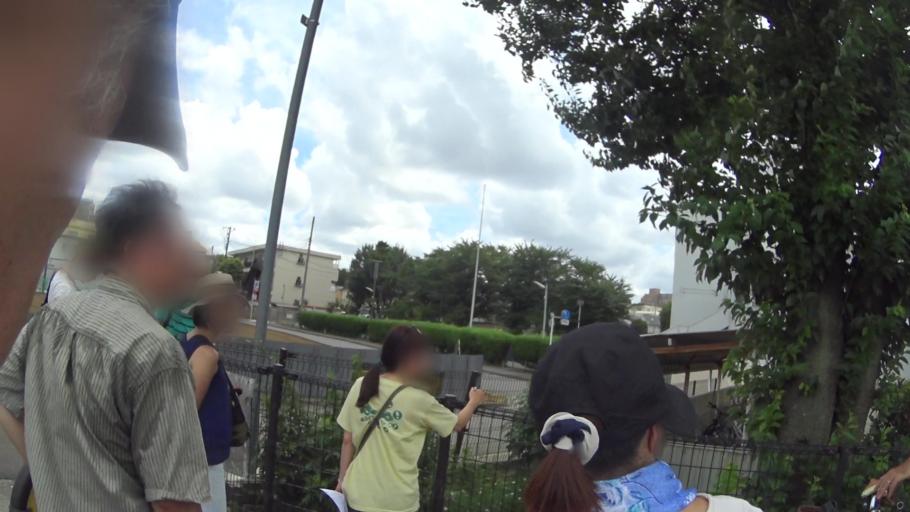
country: JP
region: Tokyo
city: Chofugaoka
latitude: 35.6545
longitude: 139.5606
